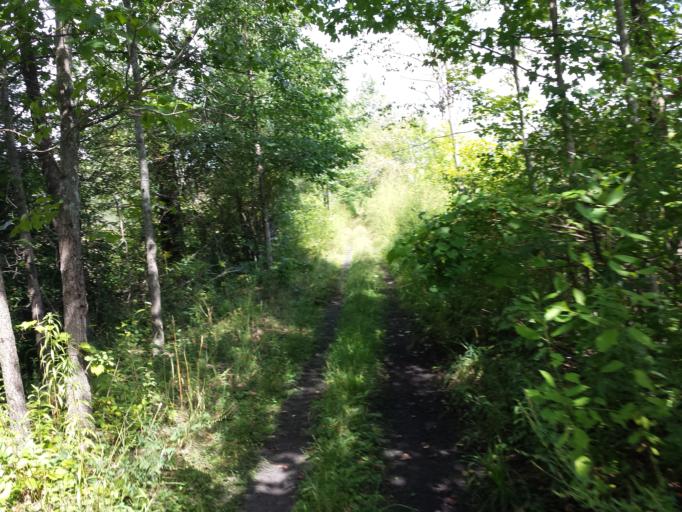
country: US
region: New York
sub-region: Tompkins County
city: East Ithaca
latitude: 42.3168
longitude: -76.3724
